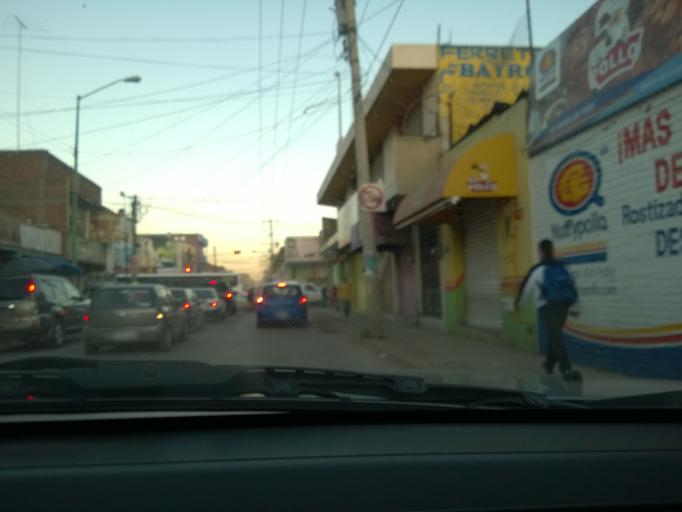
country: MX
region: Guanajuato
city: Leon
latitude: 21.1239
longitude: -101.6610
